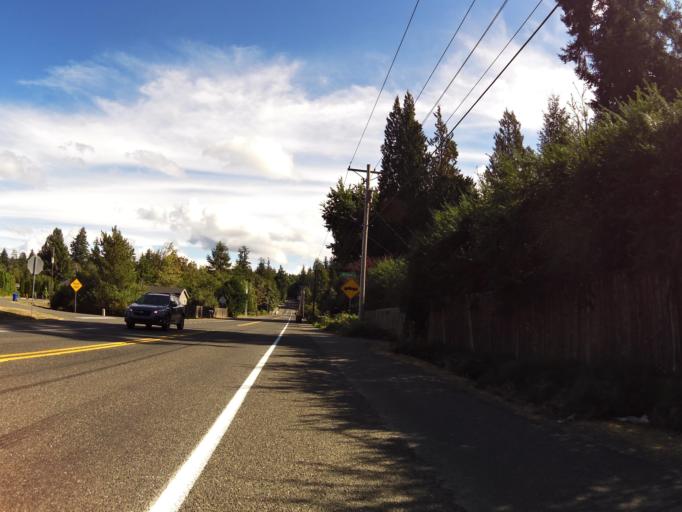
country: US
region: Washington
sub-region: Mason County
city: Shelton
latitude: 47.1279
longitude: -123.0960
